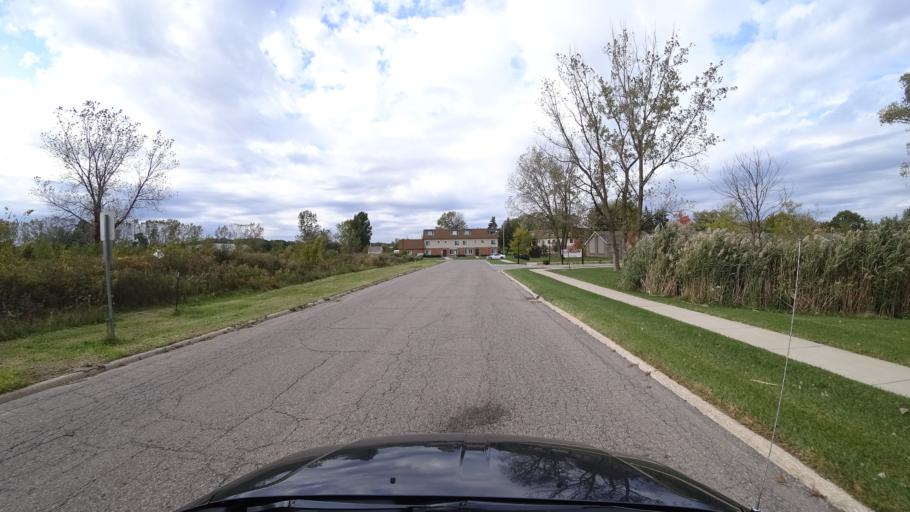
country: US
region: Indiana
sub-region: LaPorte County
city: Michigan City
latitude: 41.6687
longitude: -86.8995
